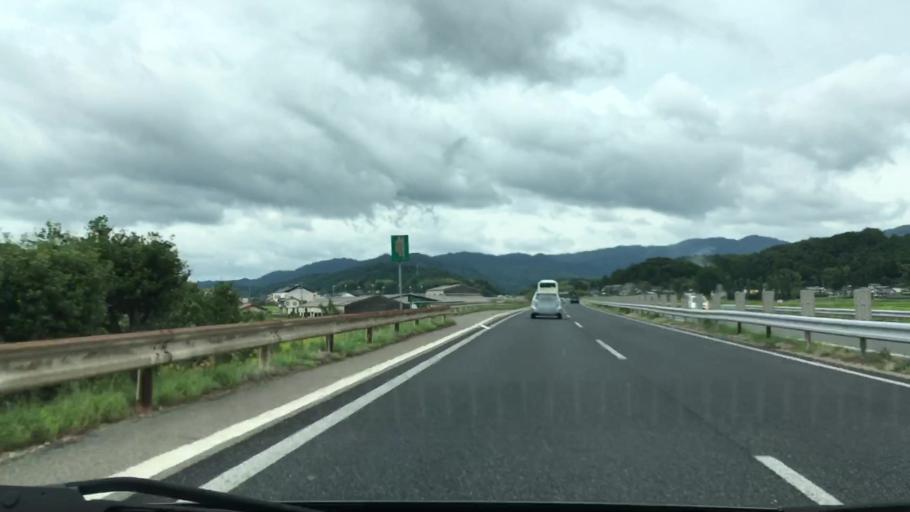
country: JP
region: Okayama
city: Tsuyama
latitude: 35.0582
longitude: 133.9104
